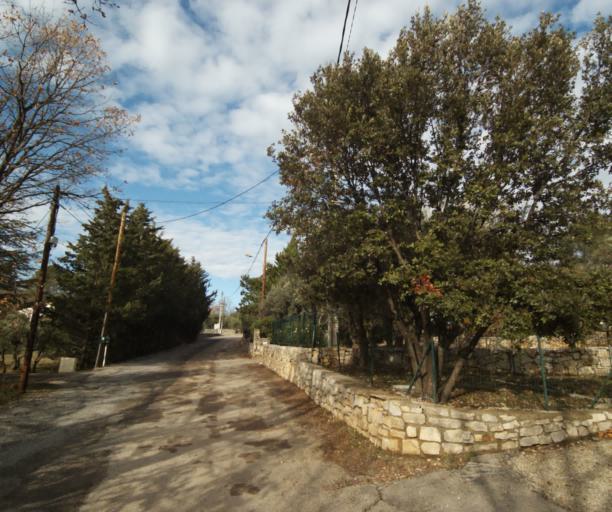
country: FR
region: Provence-Alpes-Cote d'Azur
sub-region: Departement du Var
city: Trans-en-Provence
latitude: 43.5042
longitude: 6.4793
